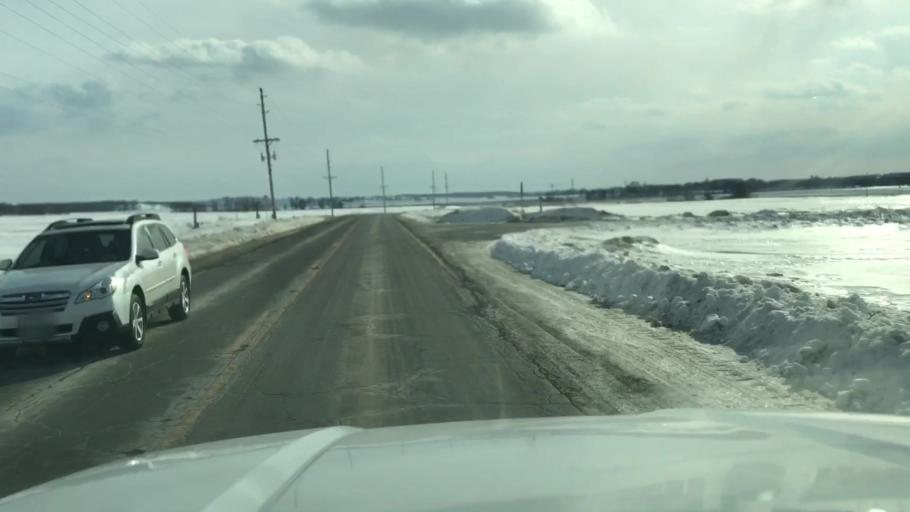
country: US
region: Missouri
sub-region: Gentry County
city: Stanberry
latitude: 40.3470
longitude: -94.6734
